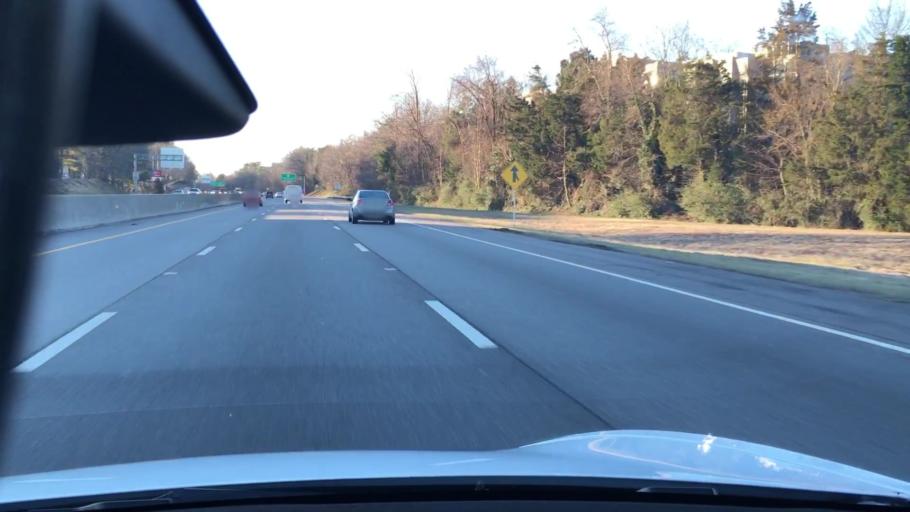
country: US
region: Virginia
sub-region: Chesterfield County
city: Bon Air
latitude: 37.5142
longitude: -77.5287
